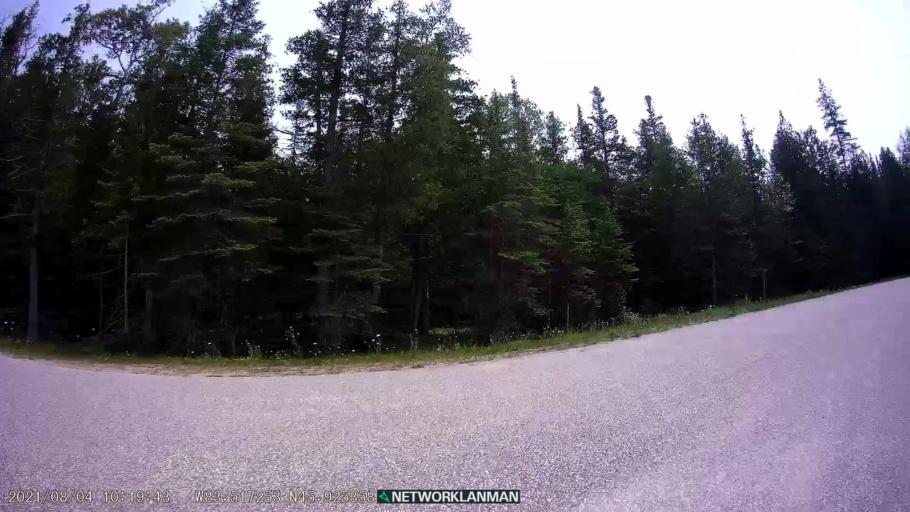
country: CA
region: Ontario
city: Thessalon
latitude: 45.9255
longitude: -83.5169
